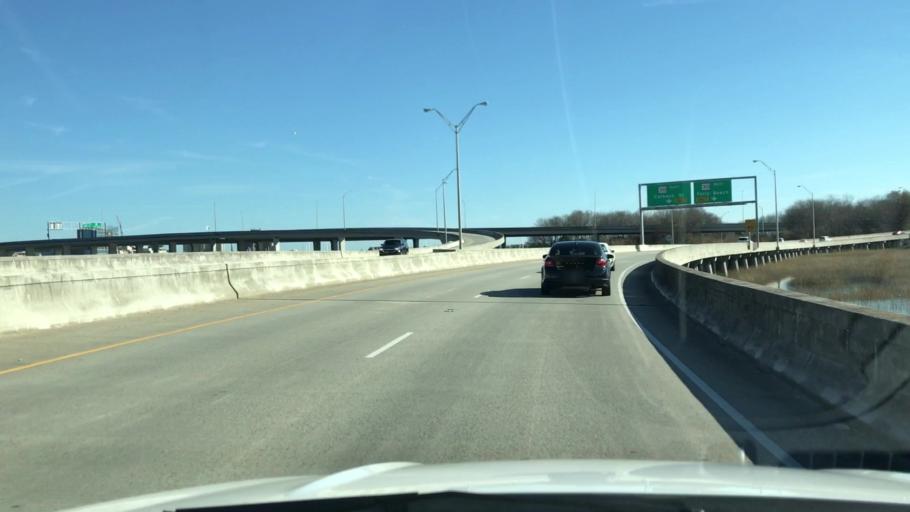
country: US
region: South Carolina
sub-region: Charleston County
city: Charleston
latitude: 32.7761
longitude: -79.9617
